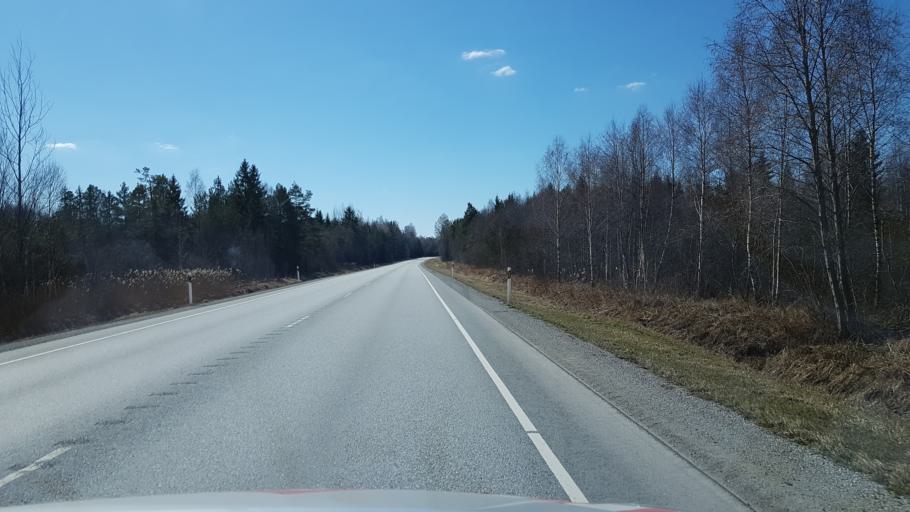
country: EE
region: Harju
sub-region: Nissi vald
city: Riisipere
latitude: 59.1552
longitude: 24.3405
